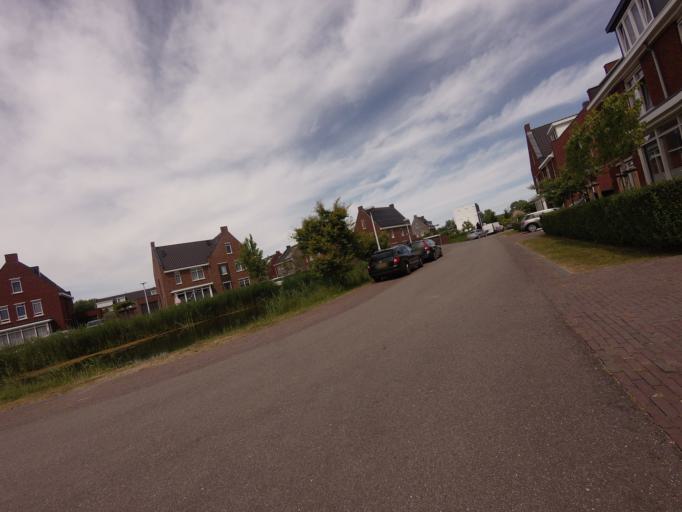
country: NL
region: Utrecht
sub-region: Stichtse Vecht
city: Spechtenkamp
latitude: 52.1005
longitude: 5.0178
